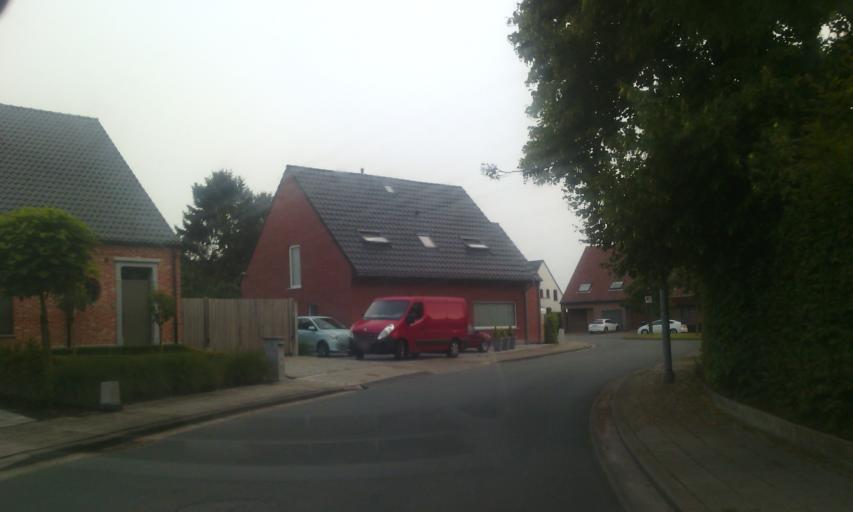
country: BE
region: Flanders
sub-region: Provincie Oost-Vlaanderen
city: Aalst
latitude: 50.9852
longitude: 4.0340
